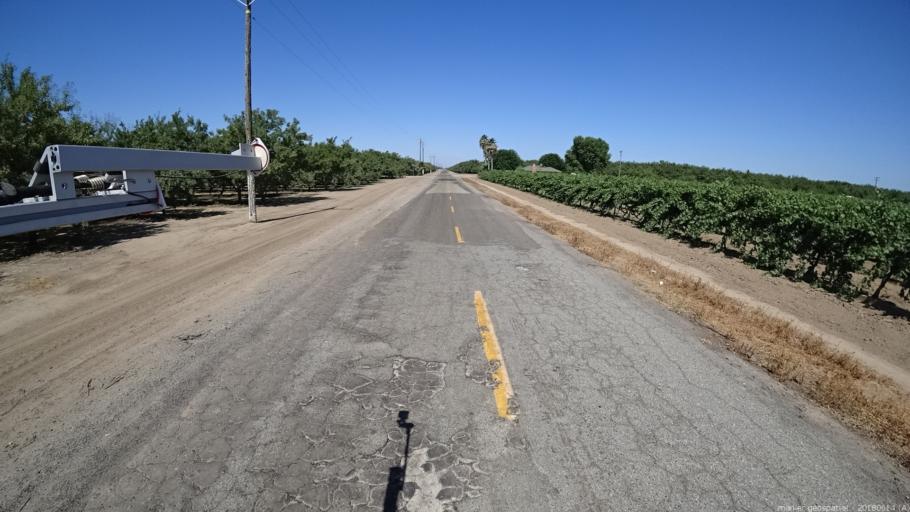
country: US
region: California
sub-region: Madera County
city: Fairmead
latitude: 36.9382
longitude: -120.2231
